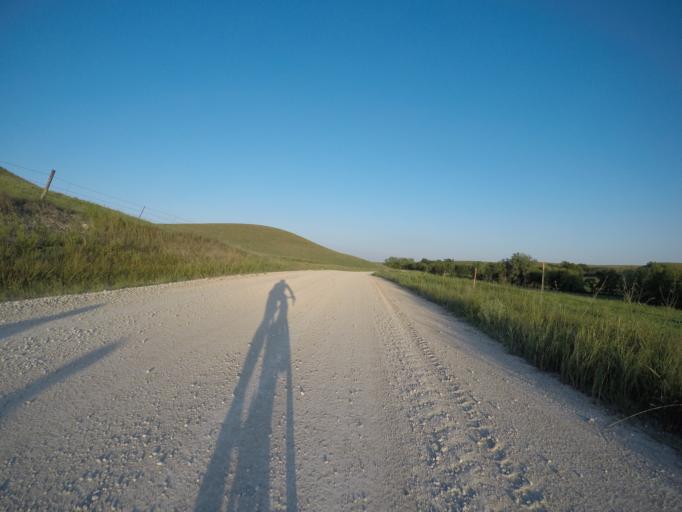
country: US
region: Kansas
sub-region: Riley County
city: Ogden
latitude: 39.0131
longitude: -96.6558
